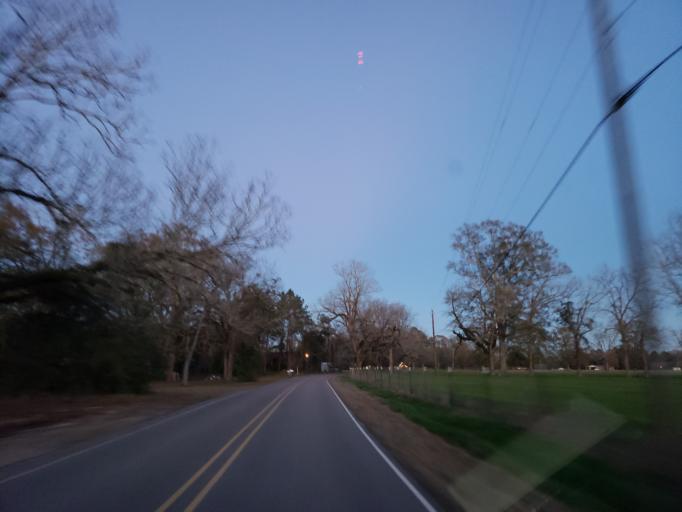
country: US
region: Mississippi
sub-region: Forrest County
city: Rawls Springs
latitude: 31.4244
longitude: -89.3430
